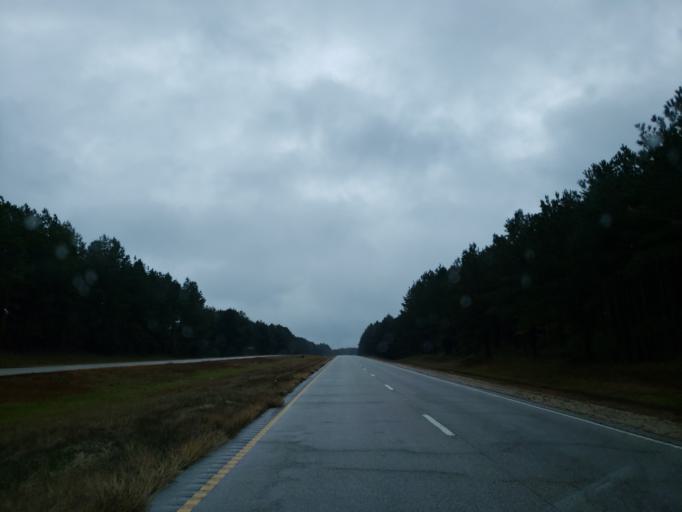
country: US
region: Mississippi
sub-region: Lauderdale County
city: Meridian
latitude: 32.2921
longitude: -88.6965
